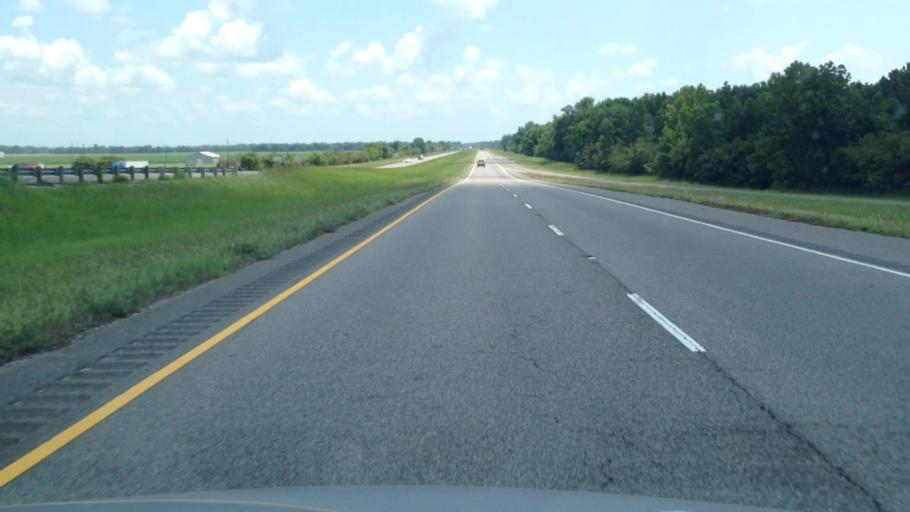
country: US
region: Louisiana
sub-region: Avoyelles Parish
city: Bunkie
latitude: 30.9506
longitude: -92.2752
